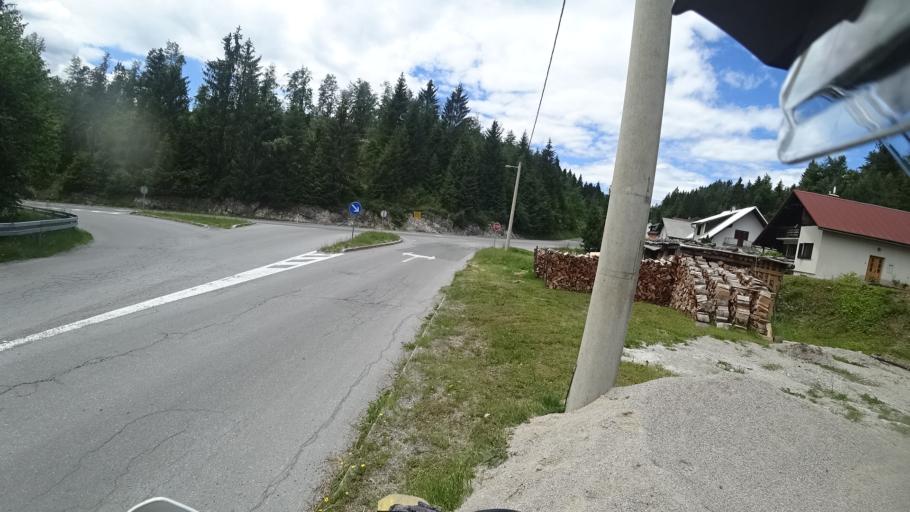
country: SI
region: Osilnica
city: Osilnica
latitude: 45.5947
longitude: 14.6238
